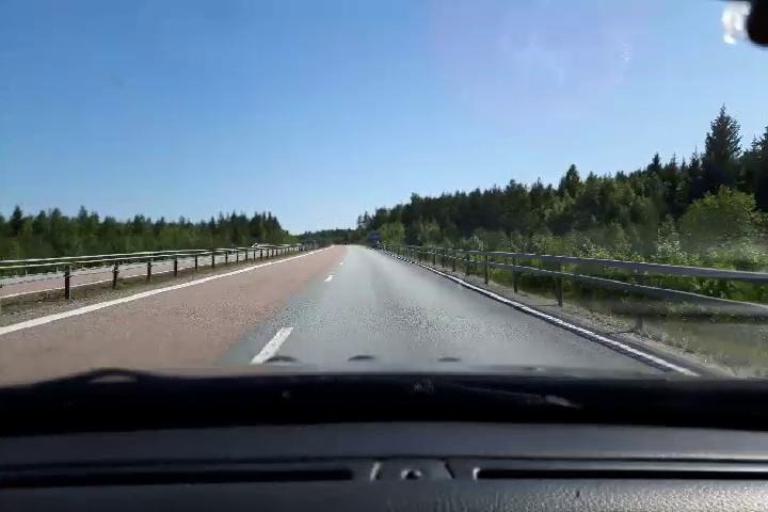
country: SE
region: Gaevleborg
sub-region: Soderhamns Kommun
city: Soderhamn
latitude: 61.4219
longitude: 16.9851
